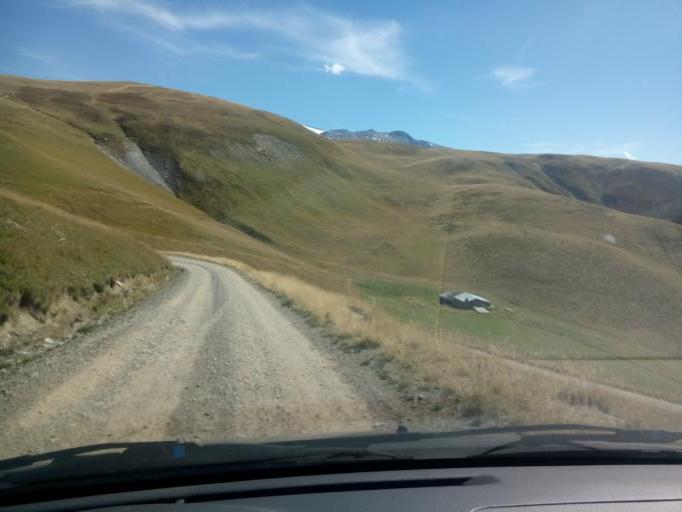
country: FR
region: Rhone-Alpes
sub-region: Departement de l'Isere
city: Mont-de-Lans
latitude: 45.0666
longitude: 6.2023
